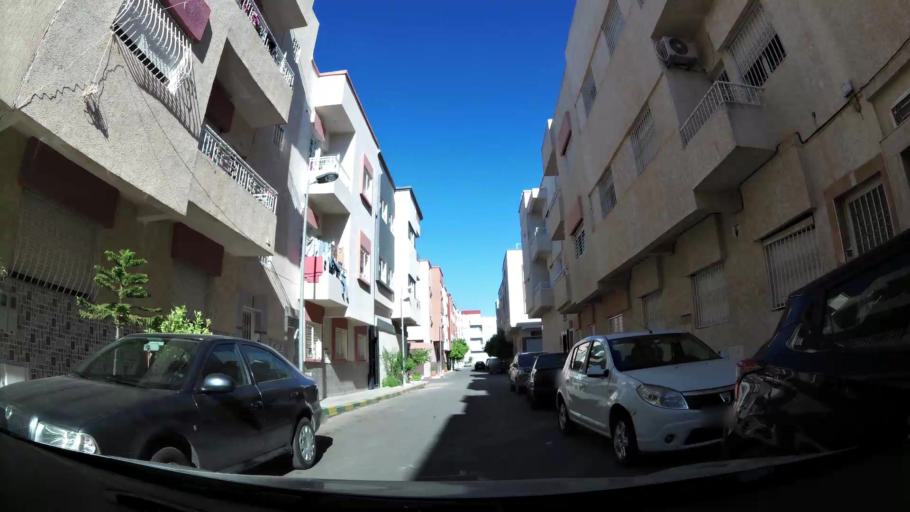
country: MA
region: Fes-Boulemane
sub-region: Fes
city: Fes
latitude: 34.0063
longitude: -5.0161
